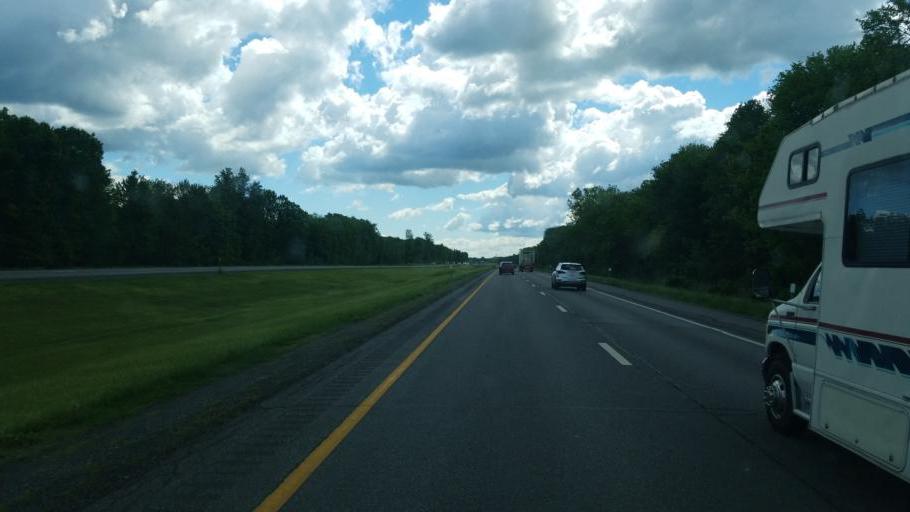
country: US
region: New York
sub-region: Madison County
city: Bolivar
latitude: 43.0916
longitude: -75.9376
